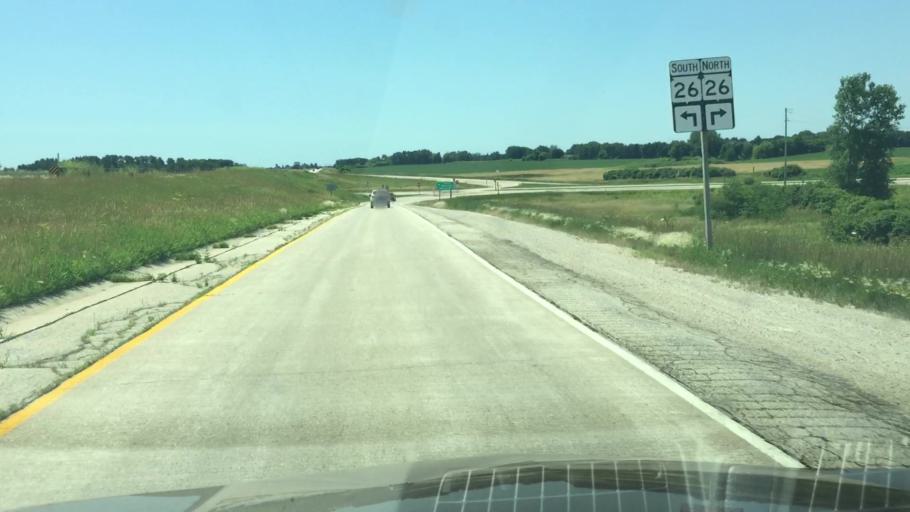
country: US
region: Wisconsin
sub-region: Fond du Lac County
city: Waupun
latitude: 43.6050
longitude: -88.7231
